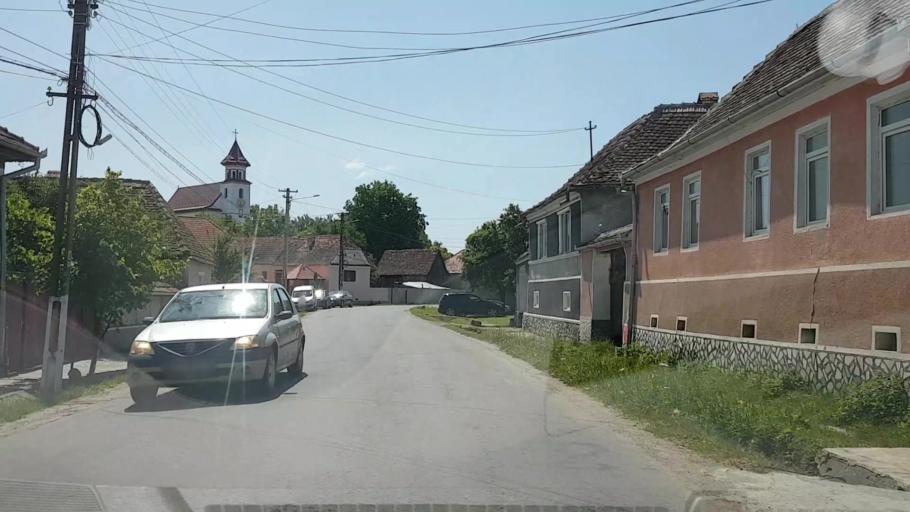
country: RO
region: Brasov
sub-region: Comuna Cincu
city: Cincu
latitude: 45.9115
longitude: 24.8086
